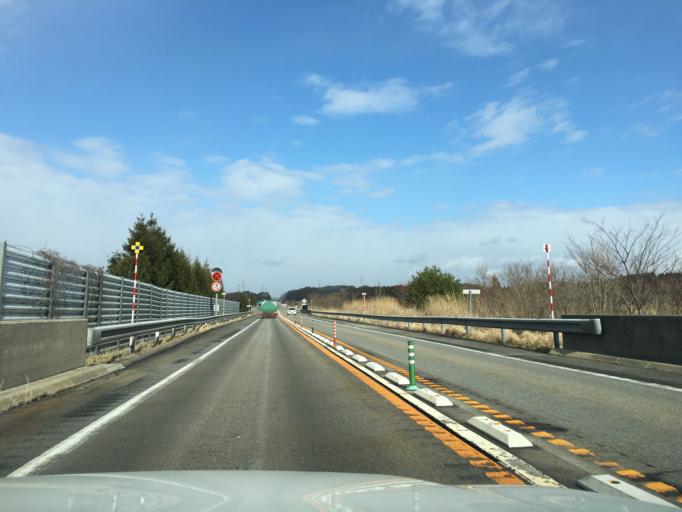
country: JP
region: Akita
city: Akita Shi
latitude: 39.7927
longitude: 140.1025
